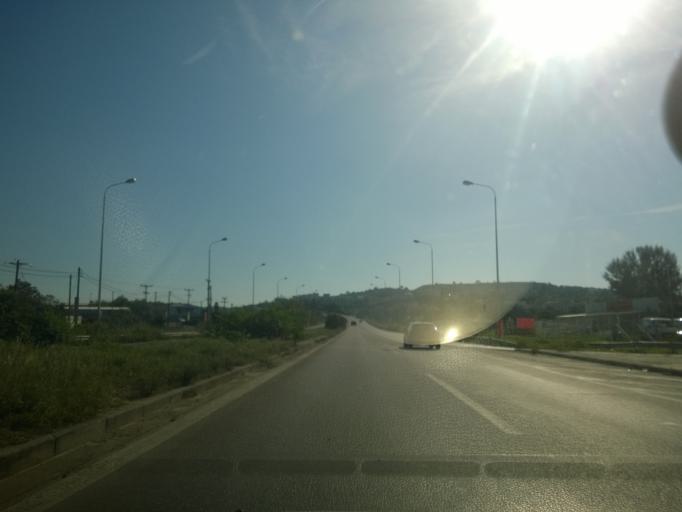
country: GR
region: Central Macedonia
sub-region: Nomos Thessalonikis
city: Neo Rysi
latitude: 40.4938
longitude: 23.0003
